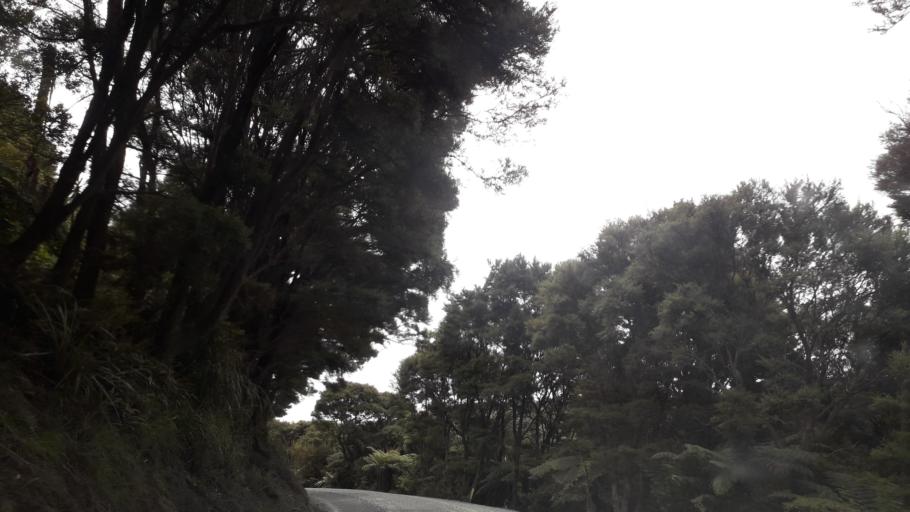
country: NZ
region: Northland
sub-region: Far North District
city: Taipa
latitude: -35.0305
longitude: 173.5625
